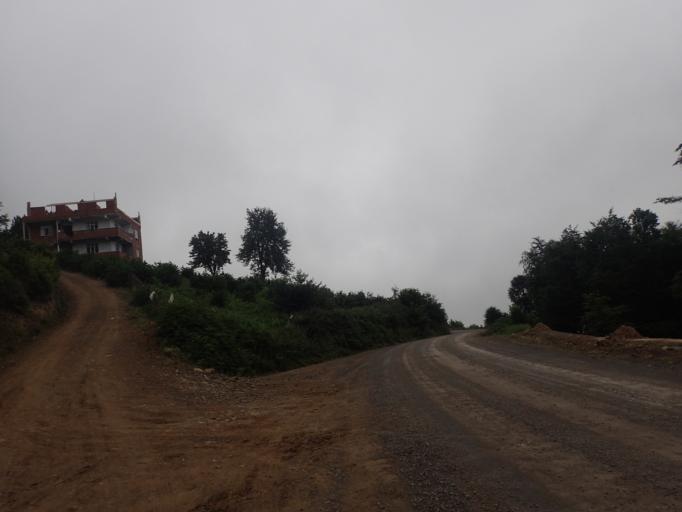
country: TR
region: Ordu
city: Akkus
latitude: 40.8500
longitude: 37.0022
